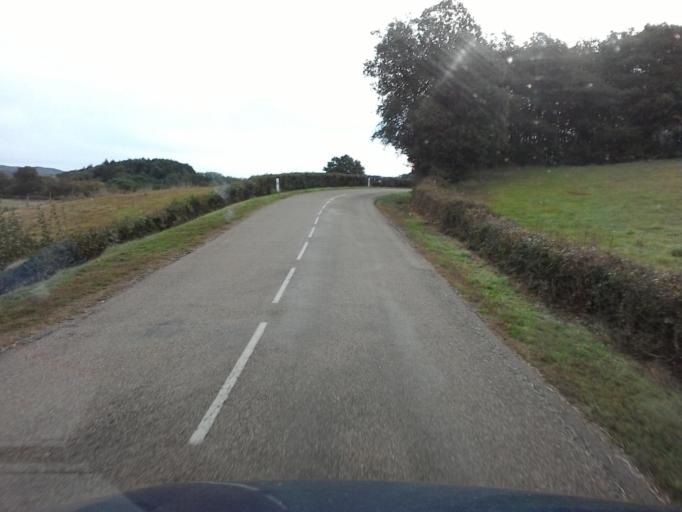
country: FR
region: Bourgogne
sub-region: Departement de la Nievre
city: Lormes
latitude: 47.2215
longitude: 3.8364
